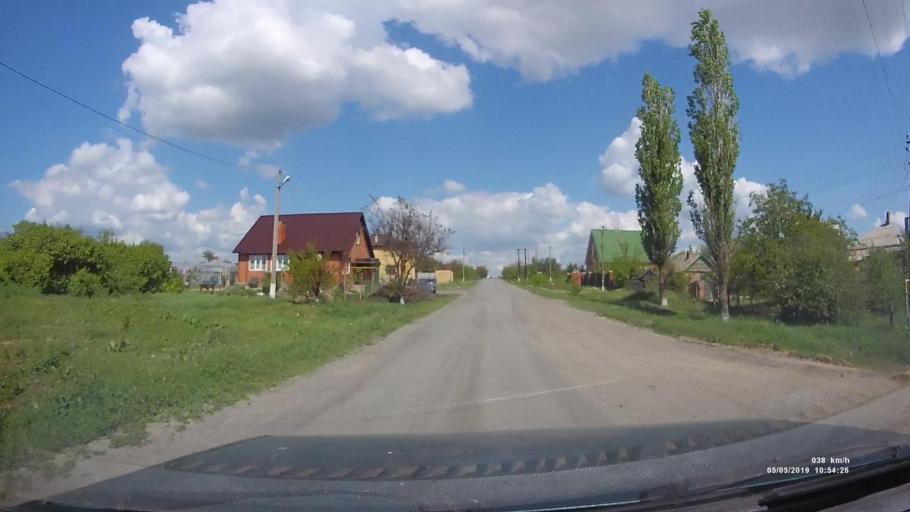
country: RU
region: Rostov
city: Ust'-Donetskiy
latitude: 47.6583
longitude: 40.8230
